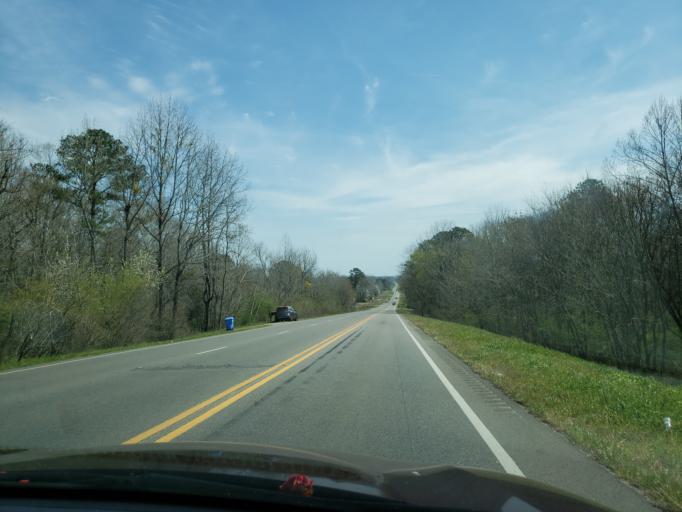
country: US
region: Alabama
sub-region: Autauga County
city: Prattville
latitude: 32.4305
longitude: -86.5295
